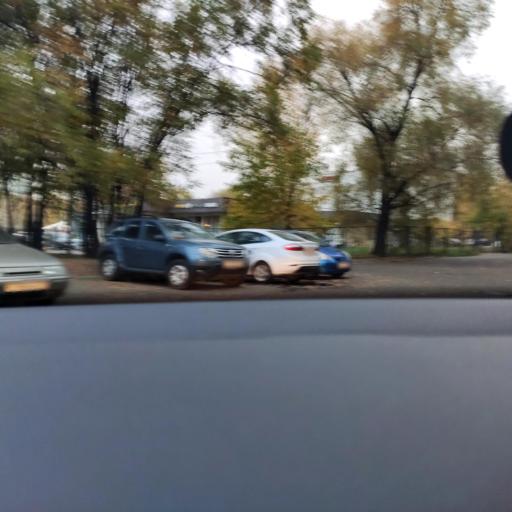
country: RU
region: Moscow
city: Orekhovo-Borisovo
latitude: 55.6298
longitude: 37.7404
